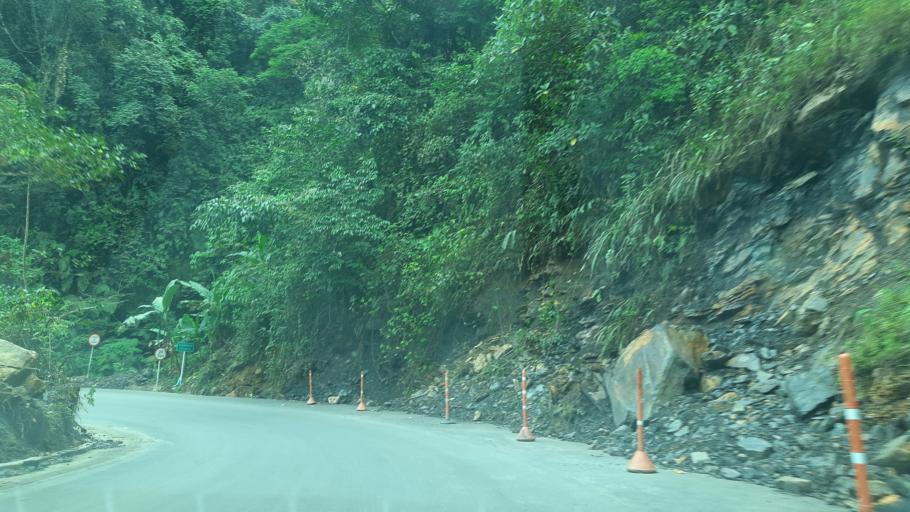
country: CO
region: Boyaca
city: Santa Maria
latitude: 4.8647
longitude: -73.2336
